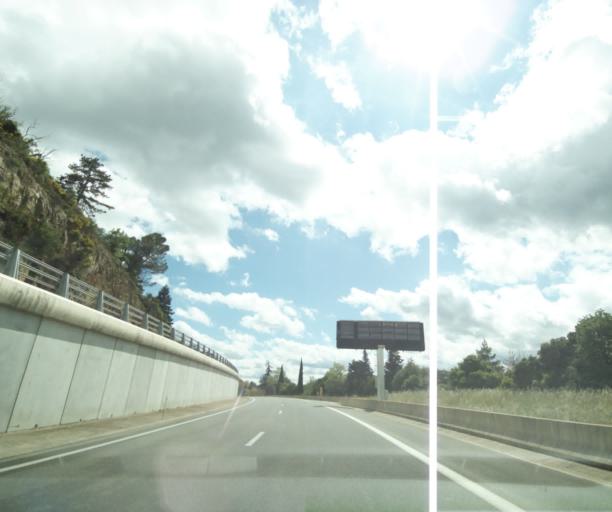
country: FR
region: Languedoc-Roussillon
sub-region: Departement de l'Herault
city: Lodeve
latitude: 43.7371
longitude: 3.3284
